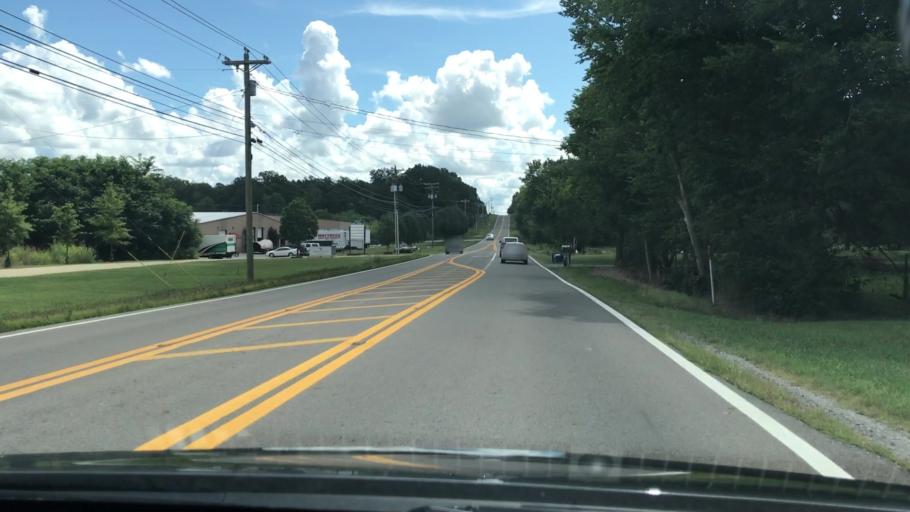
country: US
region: Tennessee
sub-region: Williamson County
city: Nolensville
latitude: 35.8494
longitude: -86.5756
